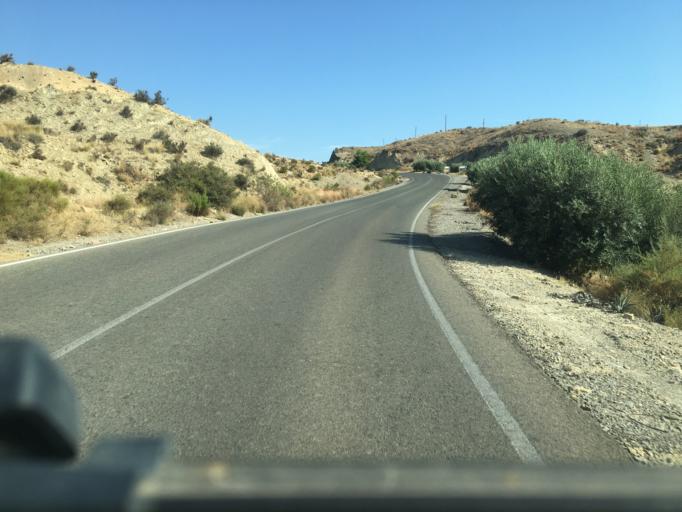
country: ES
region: Andalusia
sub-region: Provincia de Almeria
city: Huercal-Overa
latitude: 37.4294
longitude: -1.9725
